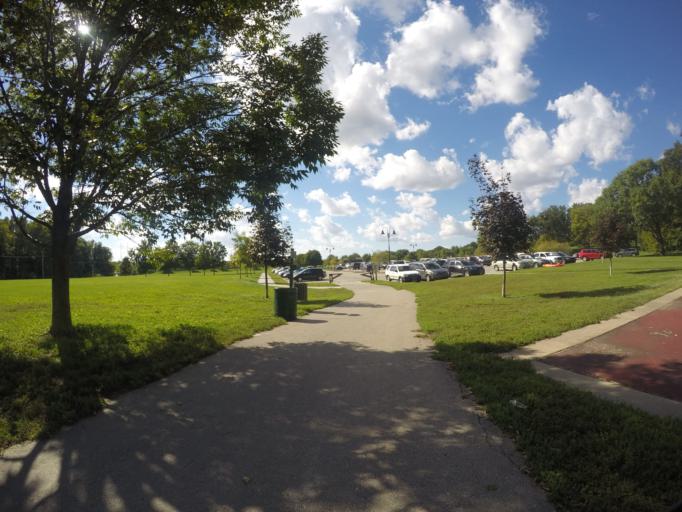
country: US
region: Kansas
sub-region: Johnson County
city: Leawood
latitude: 38.9319
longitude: -94.6137
